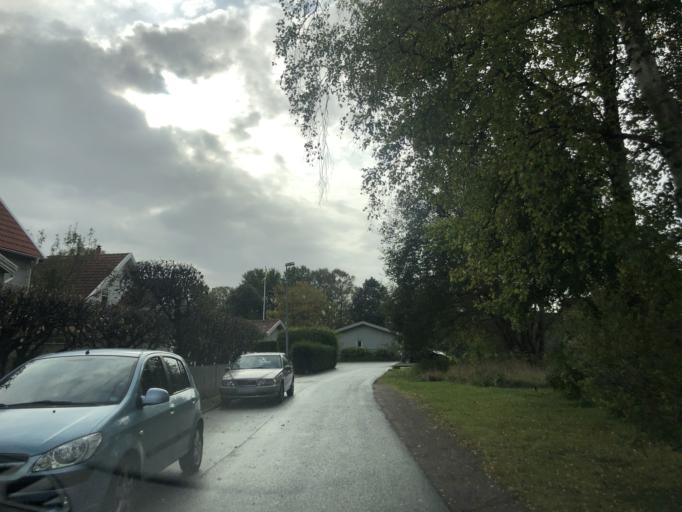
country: SE
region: Vaestra Goetaland
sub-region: Goteborg
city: Majorna
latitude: 57.6738
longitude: 11.9059
